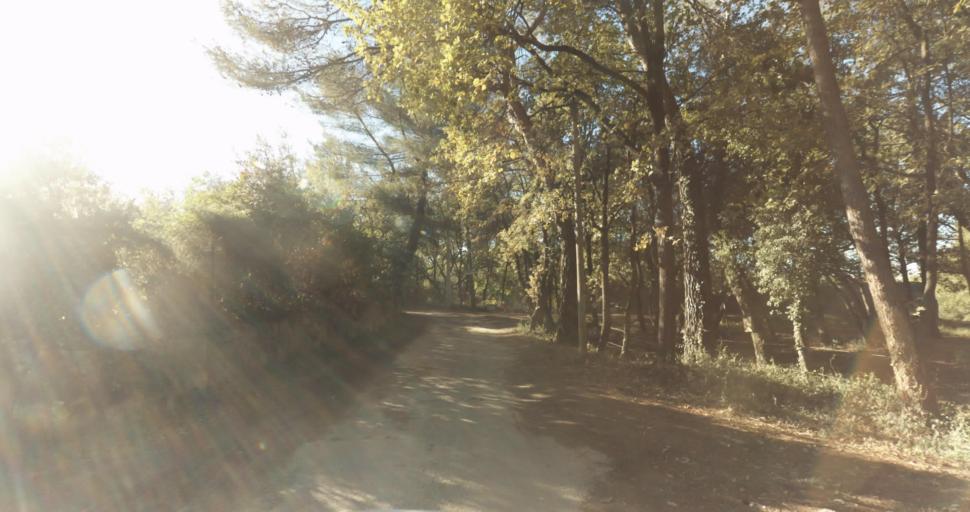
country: FR
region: Provence-Alpes-Cote d'Azur
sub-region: Departement des Alpes-Maritimes
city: La Colle-sur-Loup
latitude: 43.7106
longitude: 7.0853
